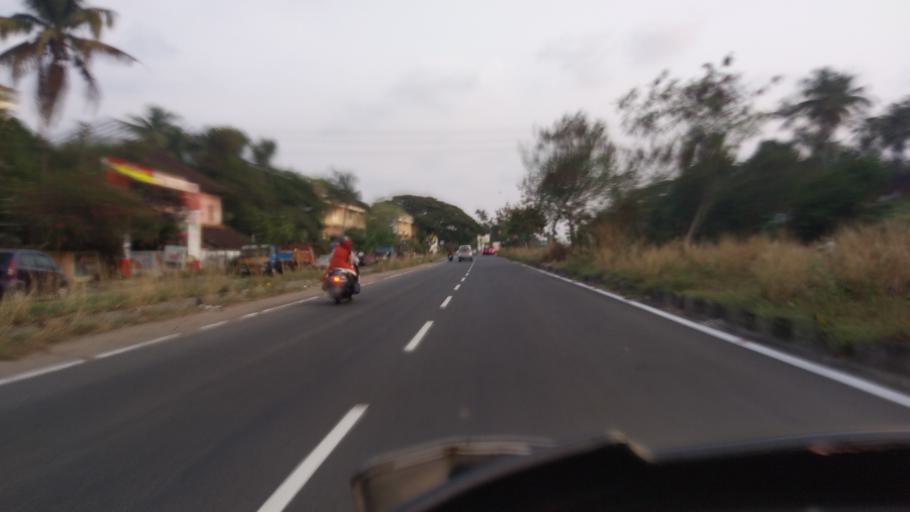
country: IN
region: Kerala
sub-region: Thrissur District
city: Kodungallur
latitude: 10.2279
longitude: 76.1956
